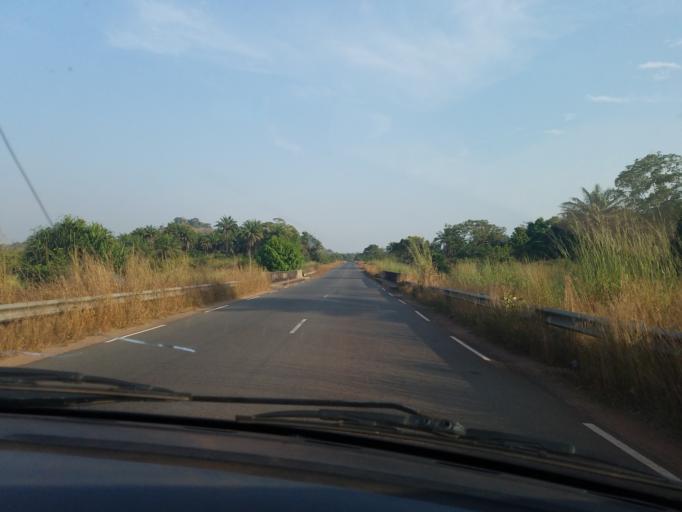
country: GN
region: Boke
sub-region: Boffa
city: Boffa
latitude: 10.3473
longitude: -14.2461
